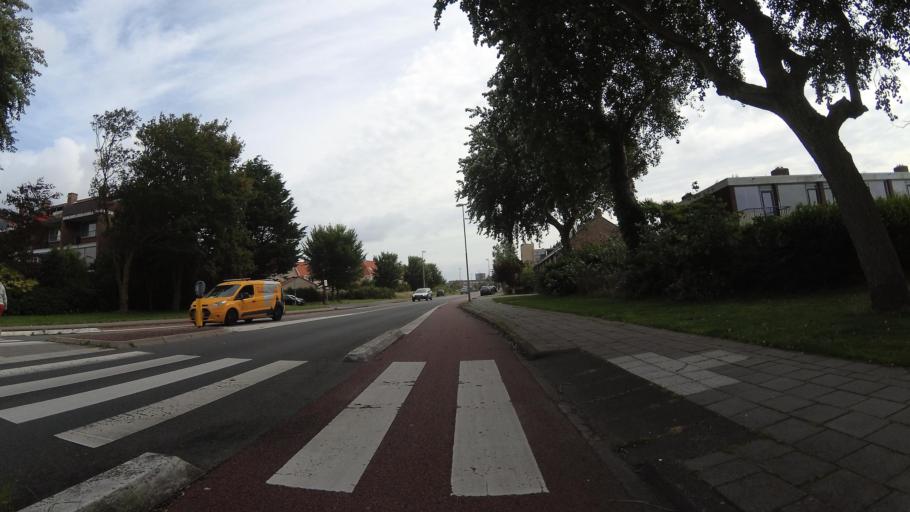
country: NL
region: North Holland
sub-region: Gemeente Den Helder
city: Den Helder
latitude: 52.9393
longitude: 4.7362
